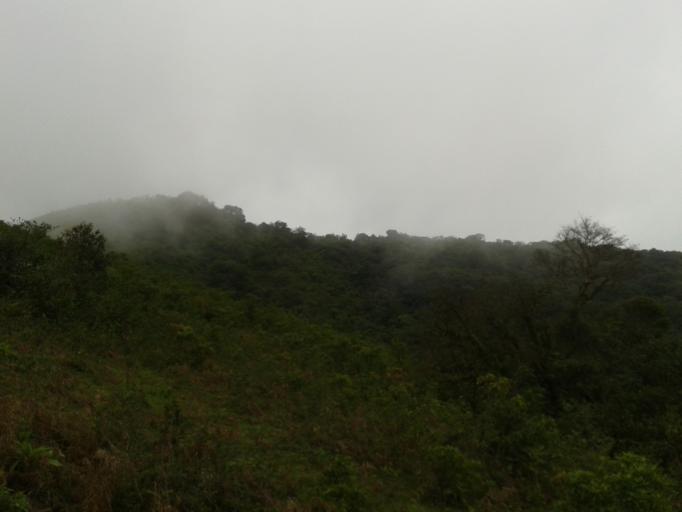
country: IN
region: Karnataka
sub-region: Chikmagalur
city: Mudigere
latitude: 12.9771
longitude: 75.6114
